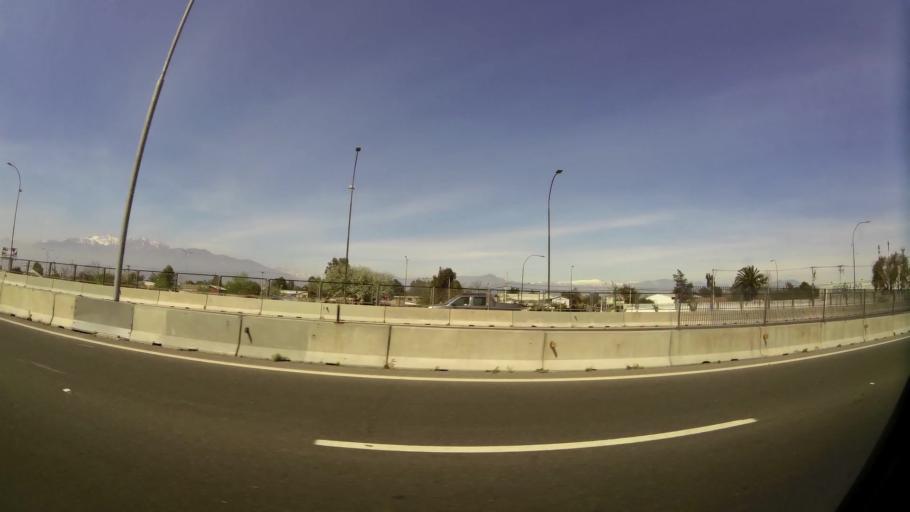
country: CL
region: Santiago Metropolitan
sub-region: Provincia de Maipo
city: San Bernardo
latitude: -33.5403
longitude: -70.6861
